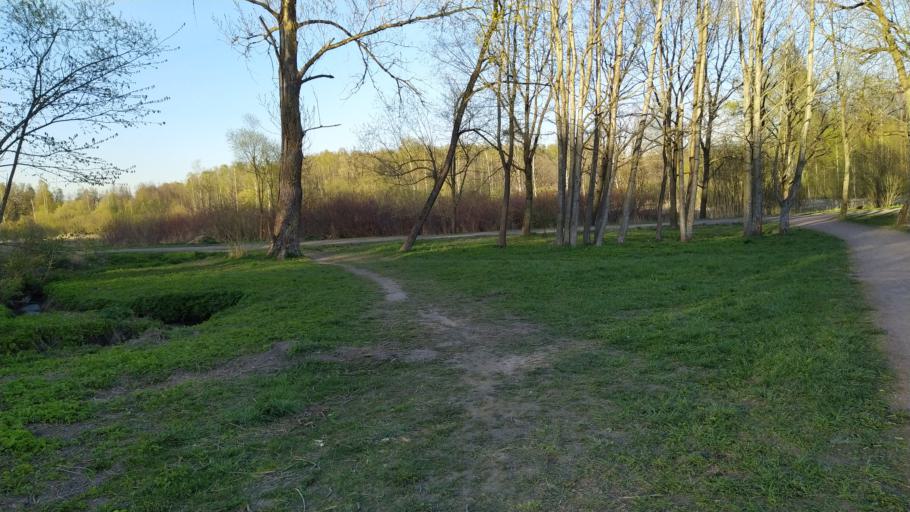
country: RU
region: St.-Petersburg
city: Pavlovsk
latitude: 59.7039
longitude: 30.4227
